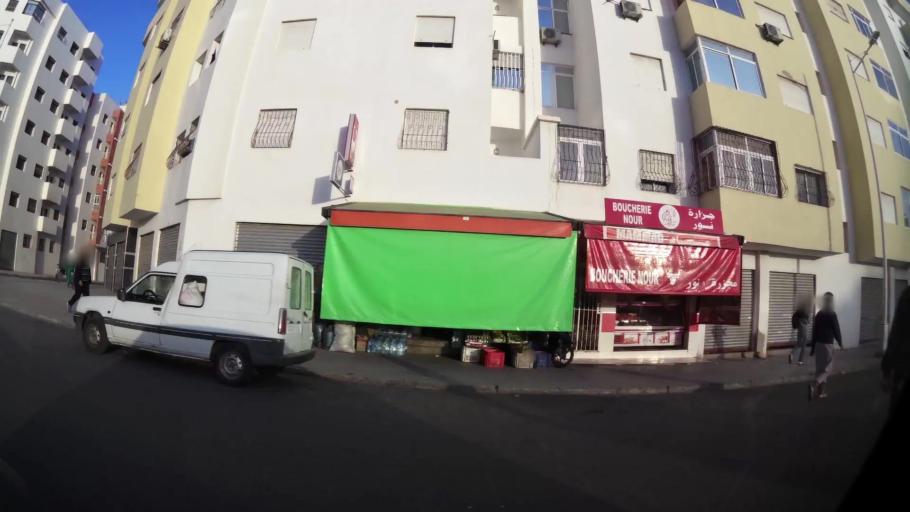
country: MA
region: Oued ed Dahab-Lagouira
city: Dakhla
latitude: 30.3994
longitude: -9.5559
